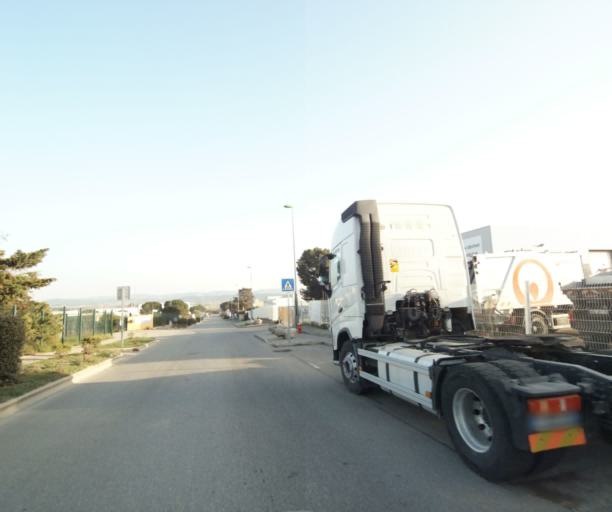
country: FR
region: Provence-Alpes-Cote d'Azur
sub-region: Departement des Bouches-du-Rhone
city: Saint-Victoret
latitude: 43.4284
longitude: 5.2408
